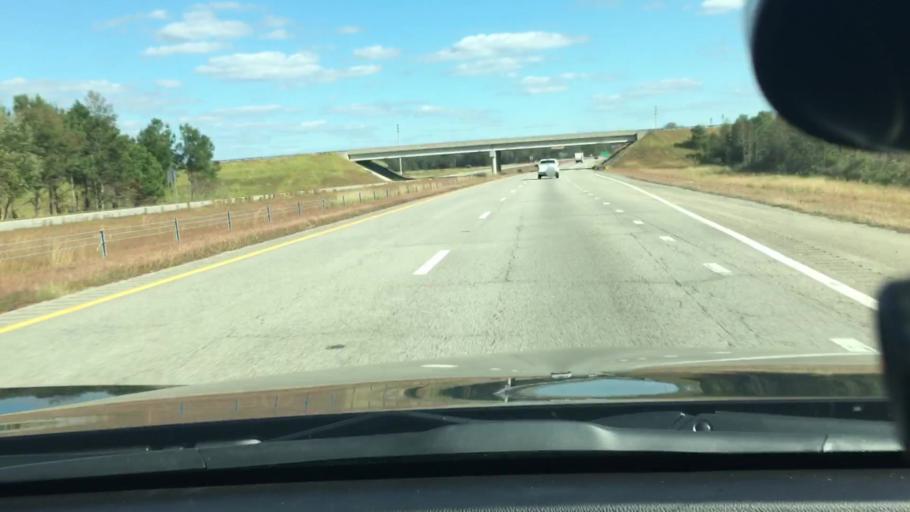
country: US
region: North Carolina
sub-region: Wilson County
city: Wilson
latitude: 35.6740
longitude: -77.9090
